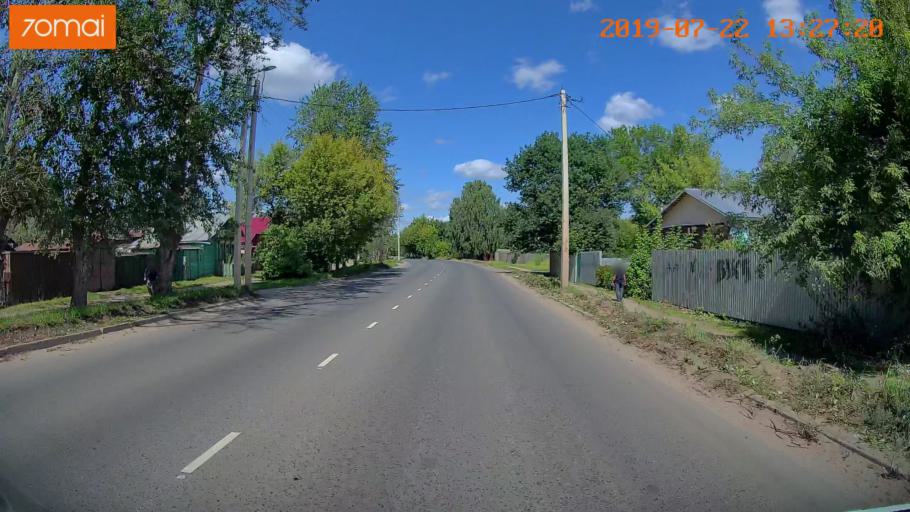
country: RU
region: Ivanovo
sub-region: Gorod Ivanovo
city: Ivanovo
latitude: 57.0339
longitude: 40.9495
